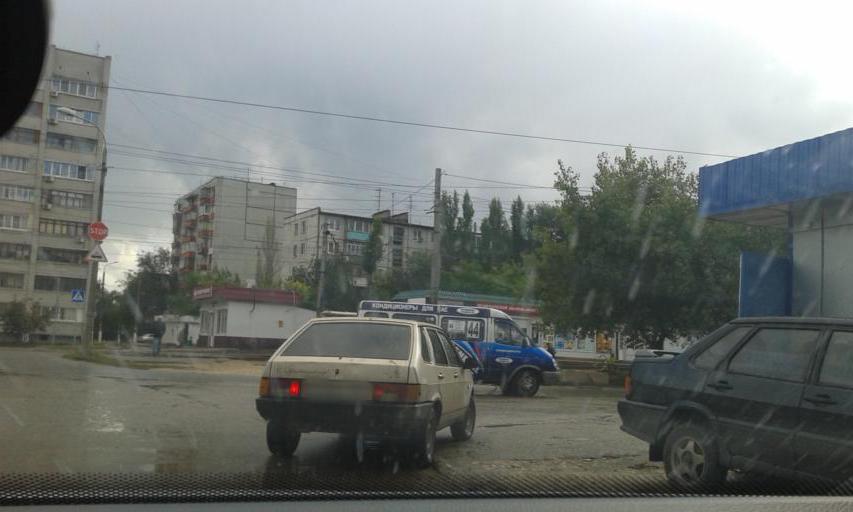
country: RU
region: Volgograd
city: Gorodishche
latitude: 48.7683
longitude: 44.4926
